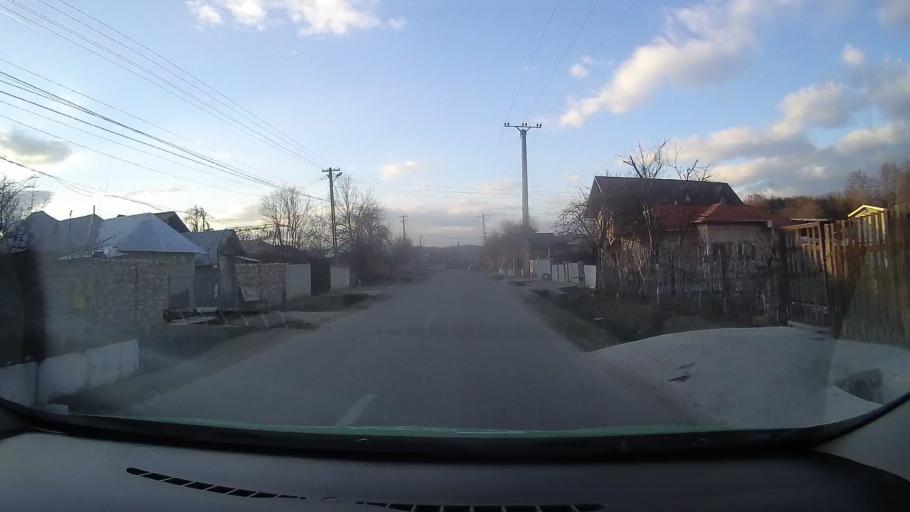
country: RO
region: Dambovita
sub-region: Comuna Gura Ocnitei
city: Adanca
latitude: 44.9263
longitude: 25.6050
